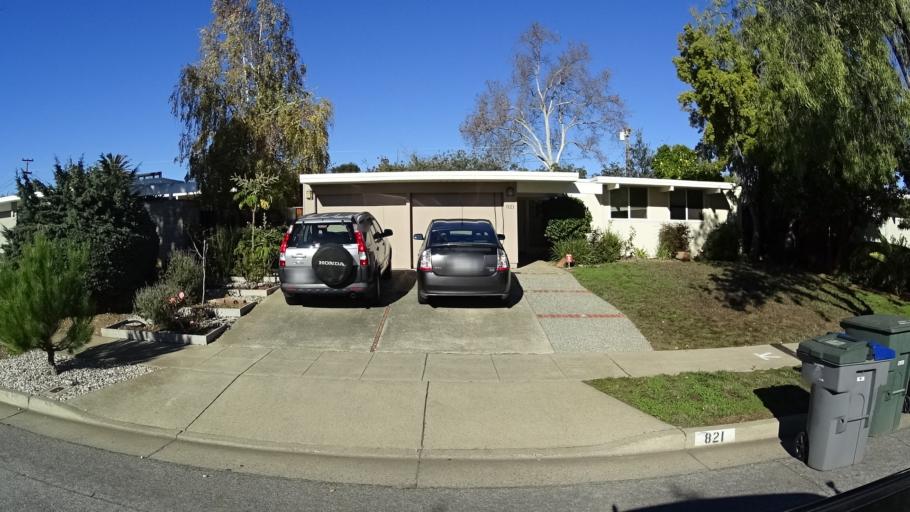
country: US
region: California
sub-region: Santa Clara County
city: Cupertino
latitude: 37.3452
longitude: -122.0179
